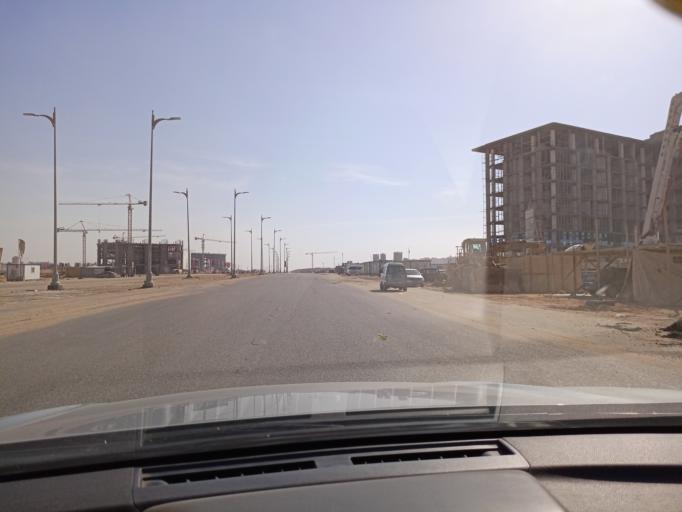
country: EG
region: Muhafazat al Qalyubiyah
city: Al Khankah
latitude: 30.0373
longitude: 31.6830
